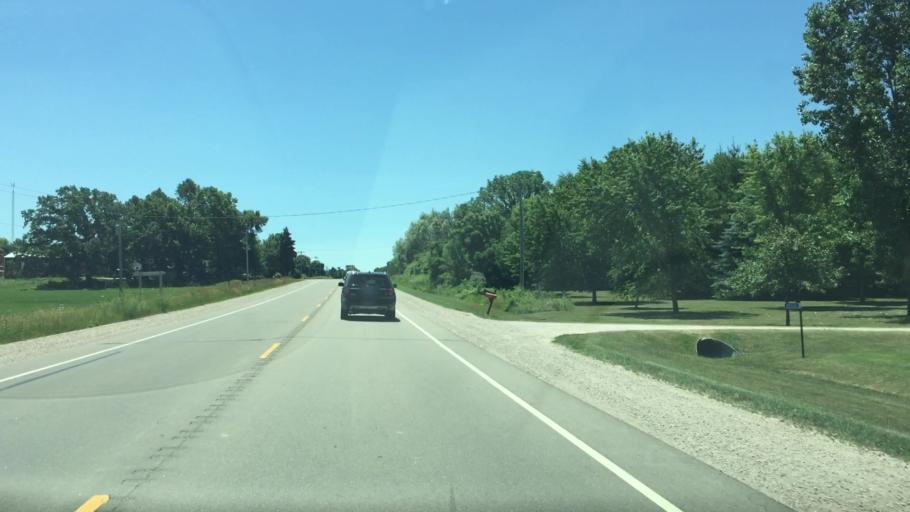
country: US
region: Wisconsin
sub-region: Calumet County
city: New Holstein
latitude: 43.9705
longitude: -88.1124
